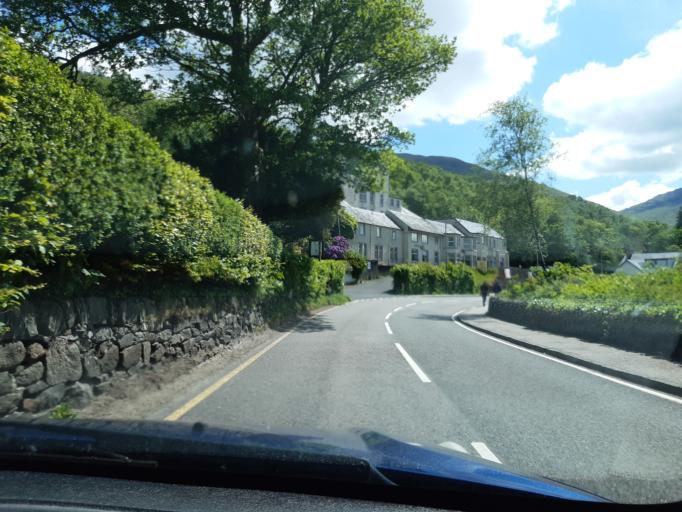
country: GB
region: Scotland
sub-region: Argyll and Bute
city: Garelochhead
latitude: 56.2051
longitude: -4.7437
